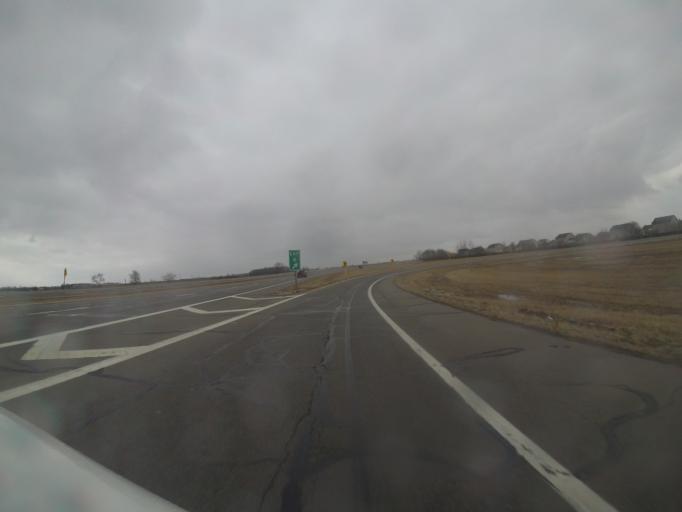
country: US
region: Ohio
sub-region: Wood County
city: Walbridge
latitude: 41.5646
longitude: -83.5100
